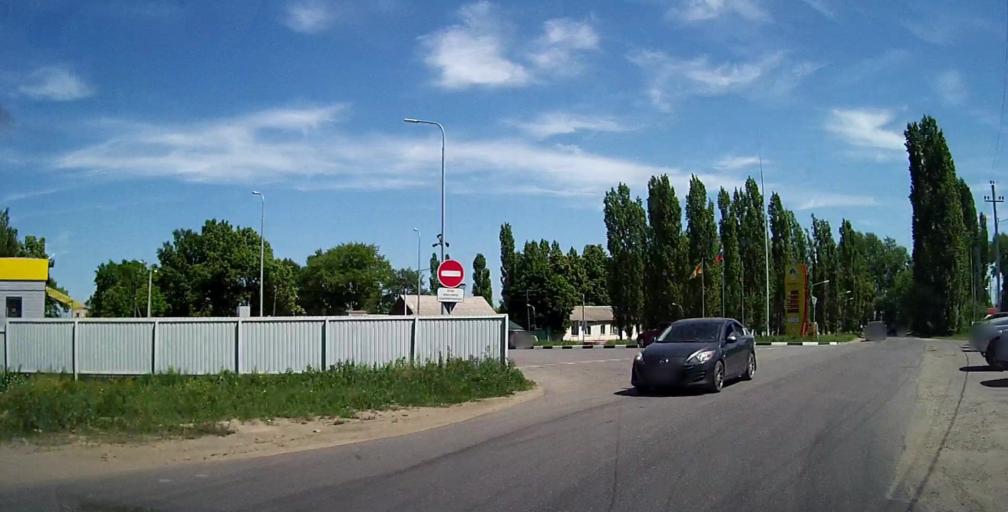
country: RU
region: Lipetsk
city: Chaplygin
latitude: 53.2487
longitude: 39.9735
